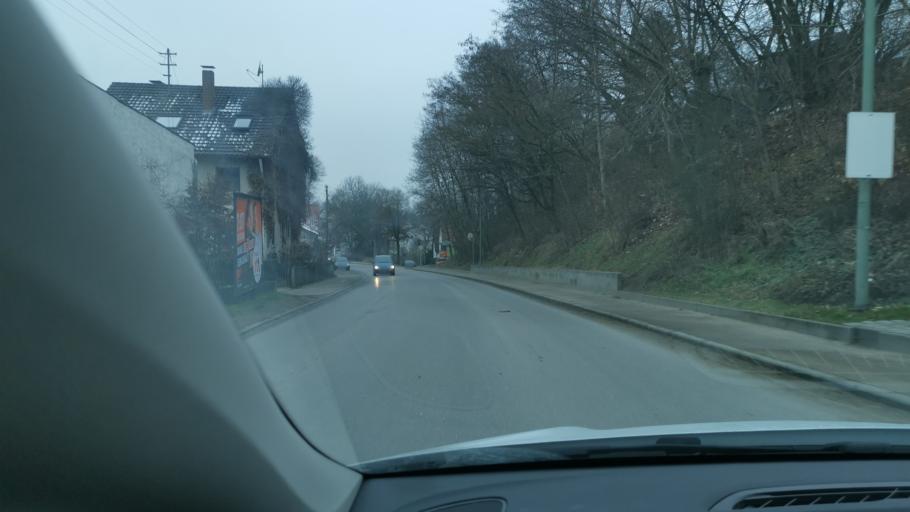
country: DE
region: Bavaria
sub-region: Swabia
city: Rehling
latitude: 48.4864
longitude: 10.9311
